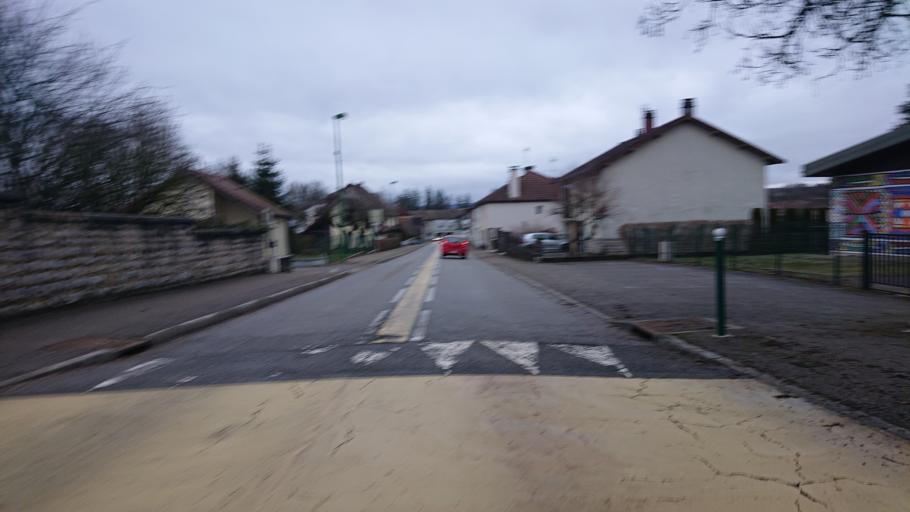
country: FR
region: Franche-Comte
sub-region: Departement du Jura
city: Clairvaux-les-Lacs
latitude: 46.5840
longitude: 5.6953
